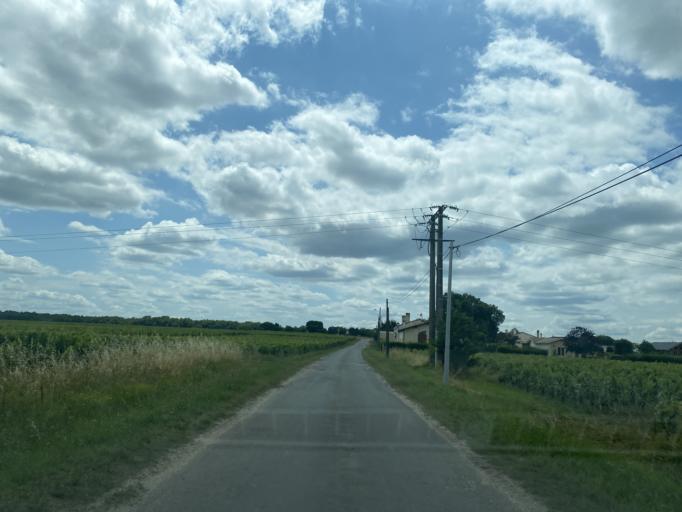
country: FR
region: Aquitaine
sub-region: Departement de la Gironde
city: Soussans
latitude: 45.0609
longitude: -0.6848
